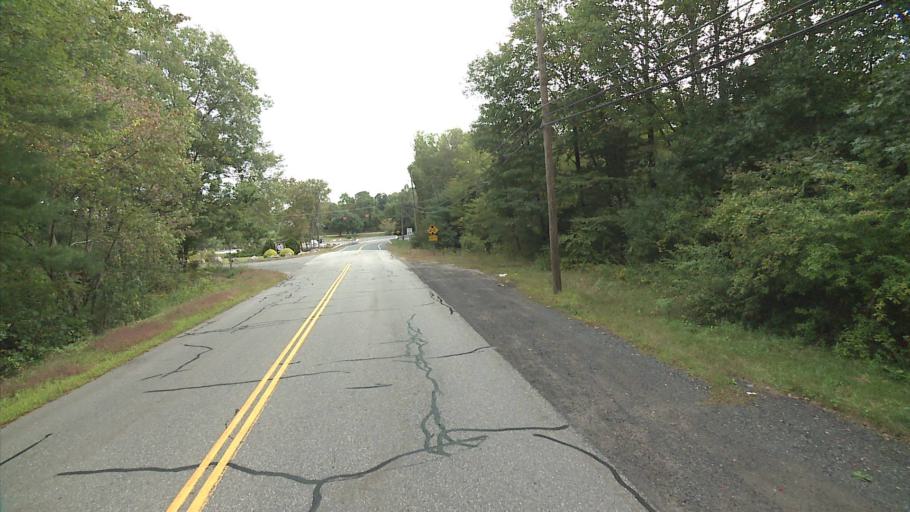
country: US
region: Connecticut
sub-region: Tolland County
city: South Coventry
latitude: 41.7834
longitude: -72.2817
